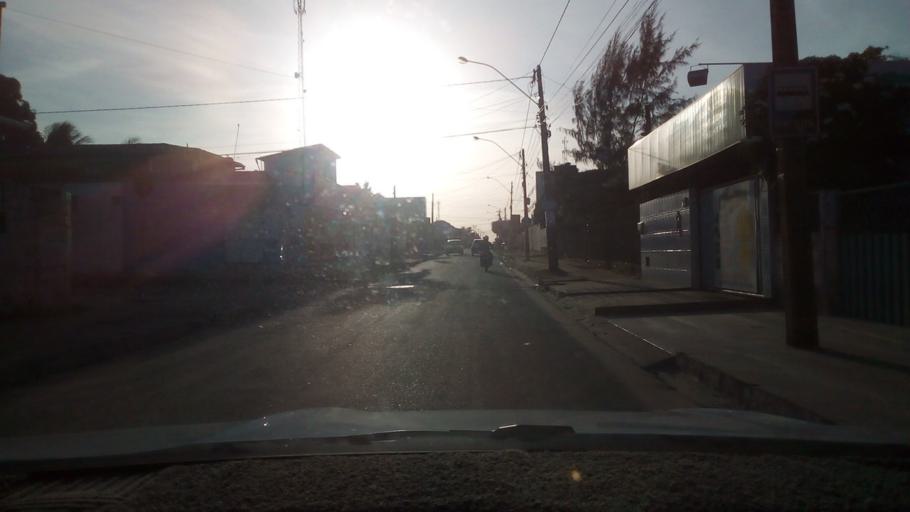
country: BR
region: Paraiba
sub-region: Conde
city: Conde
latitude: -7.1993
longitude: -34.8542
